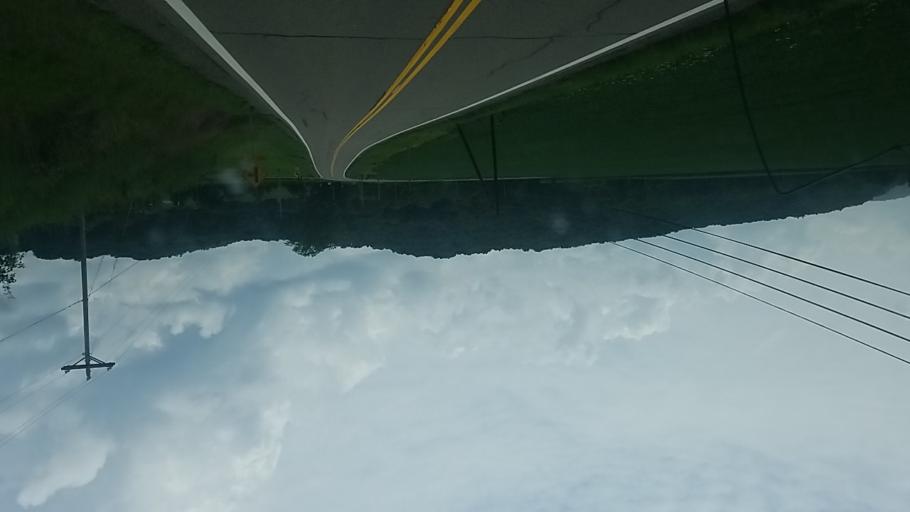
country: US
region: Ohio
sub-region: Licking County
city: Newark
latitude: 40.1622
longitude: -82.2887
